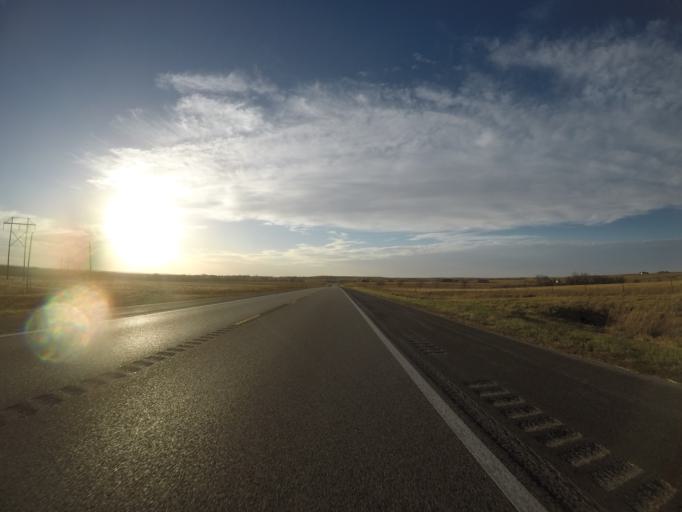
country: US
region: Kansas
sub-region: Chase County
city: Cottonwood Falls
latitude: 38.4057
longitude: -96.4789
